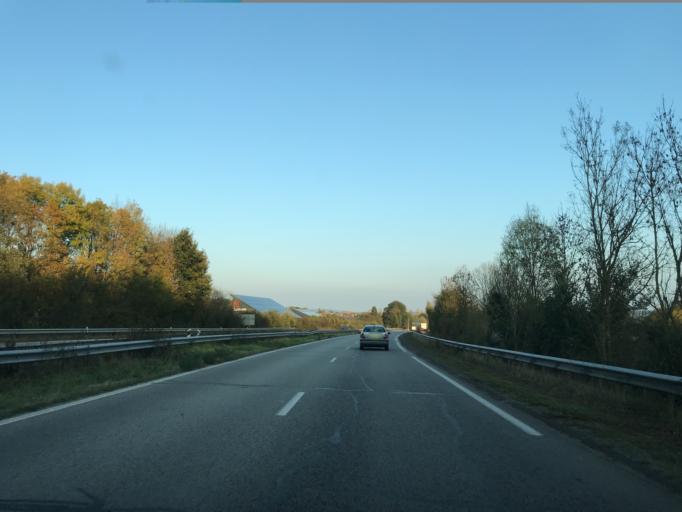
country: FR
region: Pays de la Loire
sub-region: Departement de la Sarthe
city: Mamers
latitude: 48.5099
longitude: 0.3386
